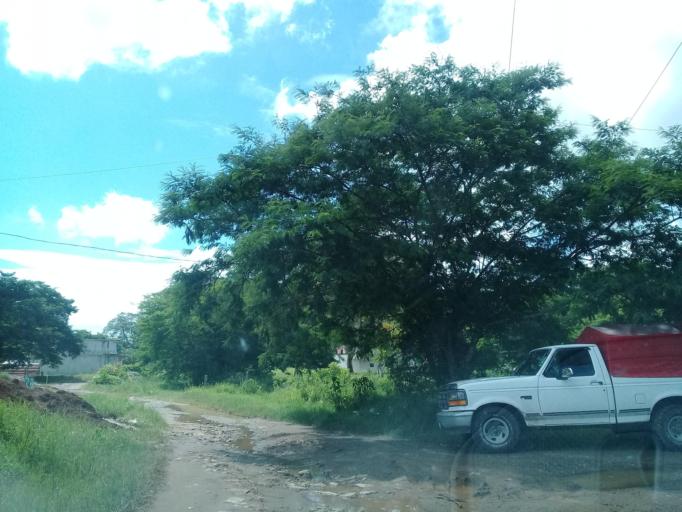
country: MX
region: Veracruz
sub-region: Jilotepec
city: El Pueblito (Garbanzal)
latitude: 19.5732
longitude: -96.8957
